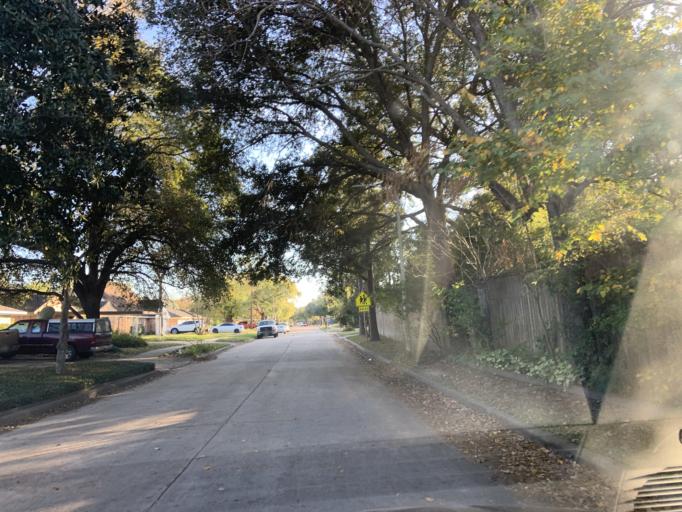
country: US
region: Texas
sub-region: Harris County
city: Bellaire
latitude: 29.6900
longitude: -95.5189
